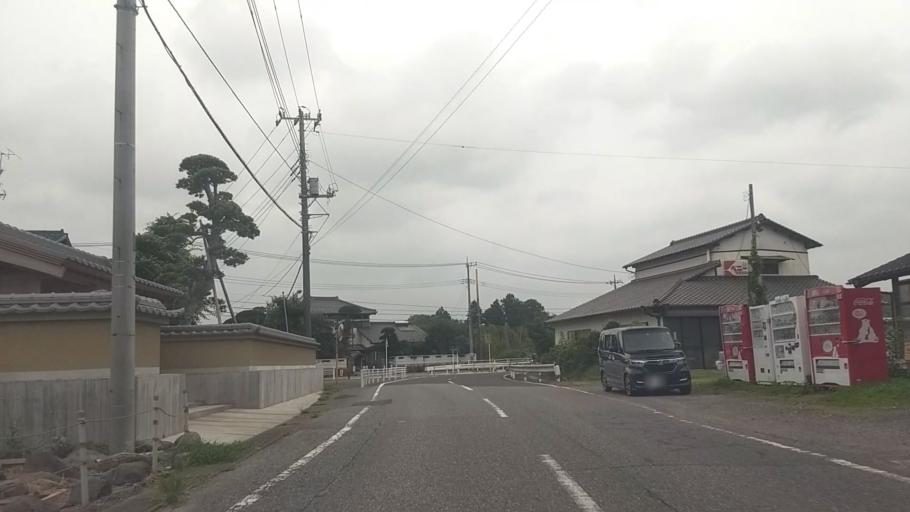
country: JP
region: Chiba
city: Kisarazu
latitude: 35.3755
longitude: 140.0143
